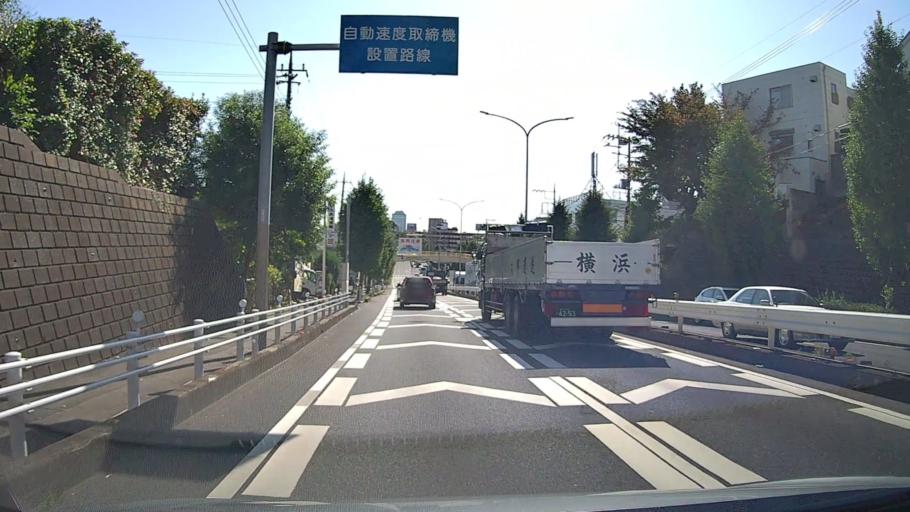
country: JP
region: Saitama
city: Wako
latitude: 35.7739
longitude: 139.6200
